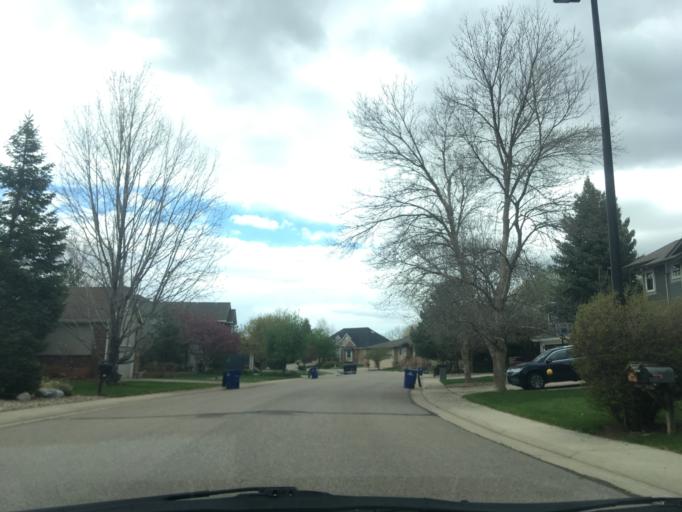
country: US
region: Colorado
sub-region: Boulder County
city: Louisville
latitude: 40.0225
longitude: -105.1260
